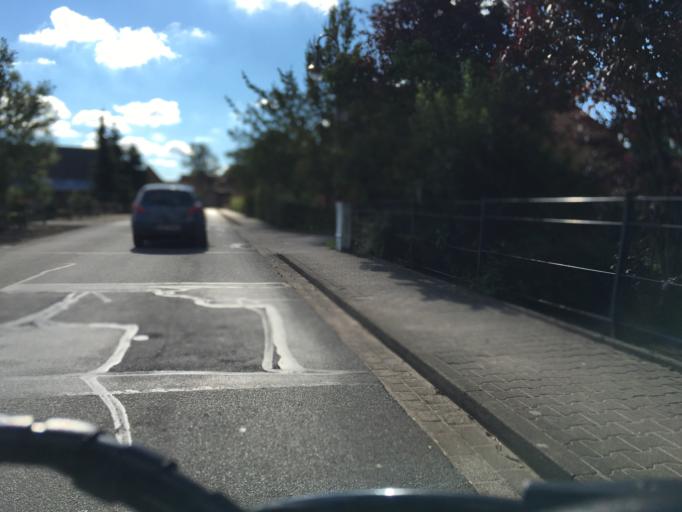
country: DE
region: Lower Saxony
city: Bardowick
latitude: 53.3036
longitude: 10.3912
